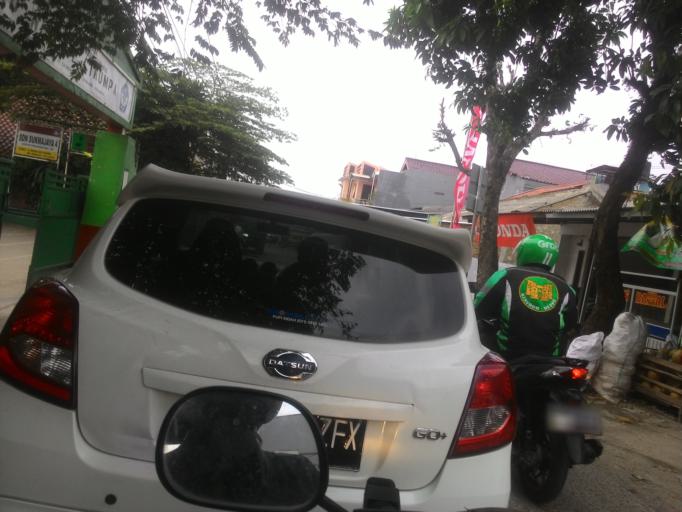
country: ID
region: West Java
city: Depok
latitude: -6.4228
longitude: 106.8377
